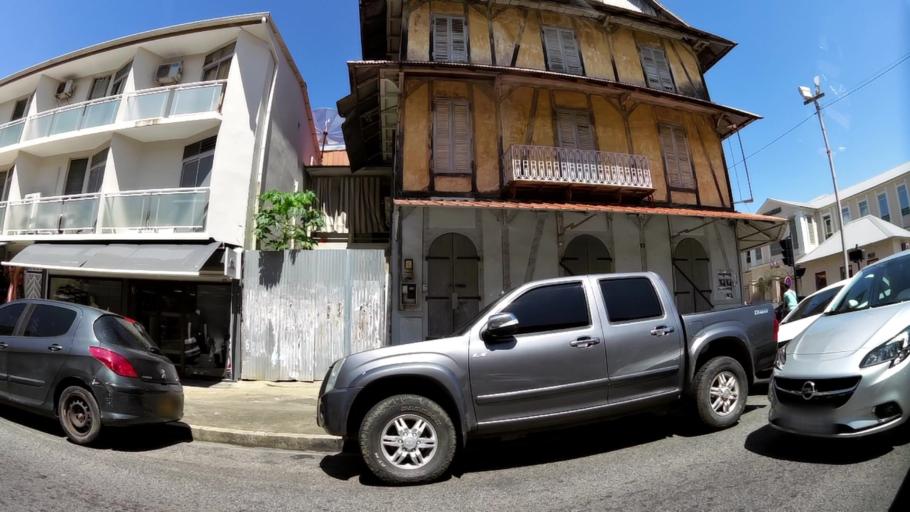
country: GF
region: Guyane
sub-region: Guyane
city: Cayenne
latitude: 4.9387
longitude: -52.3317
